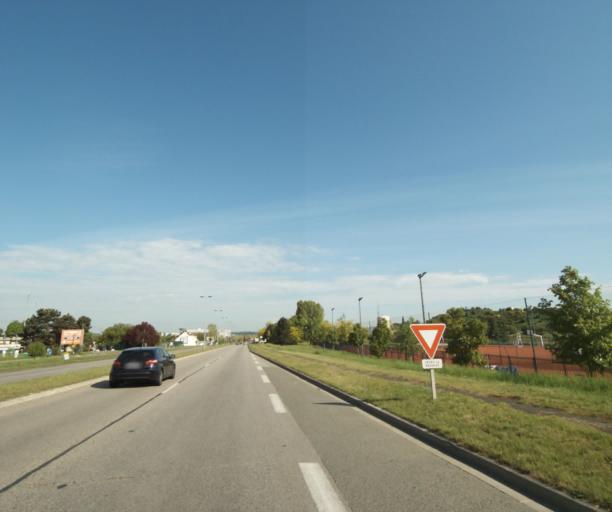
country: FR
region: Ile-de-France
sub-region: Departement des Yvelines
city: Chapet
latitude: 48.9704
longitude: 1.9200
